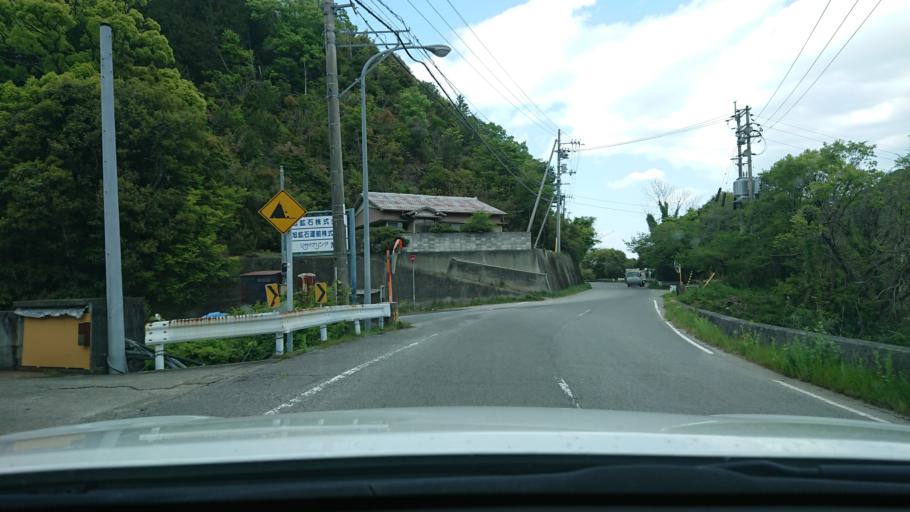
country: JP
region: Tokushima
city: Komatsushimacho
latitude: 33.9831
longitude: 134.5436
